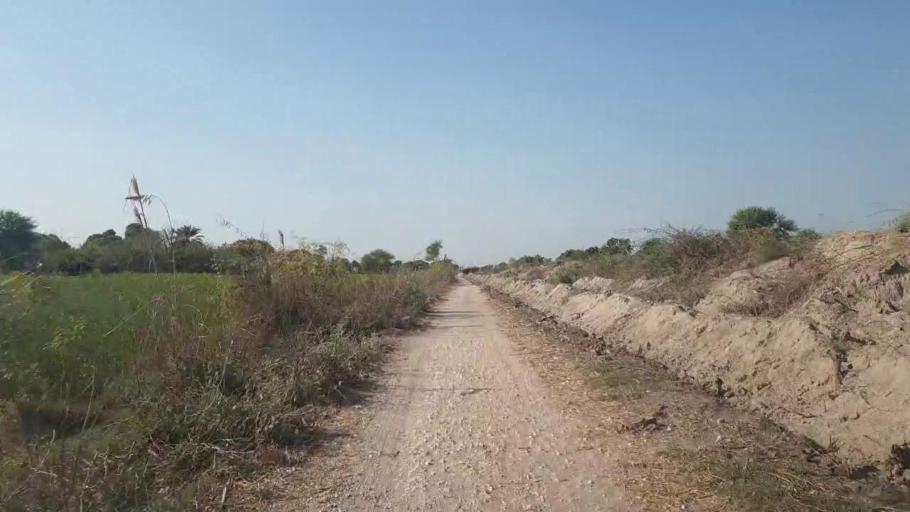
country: PK
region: Sindh
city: Chambar
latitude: 25.3042
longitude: 68.7853
